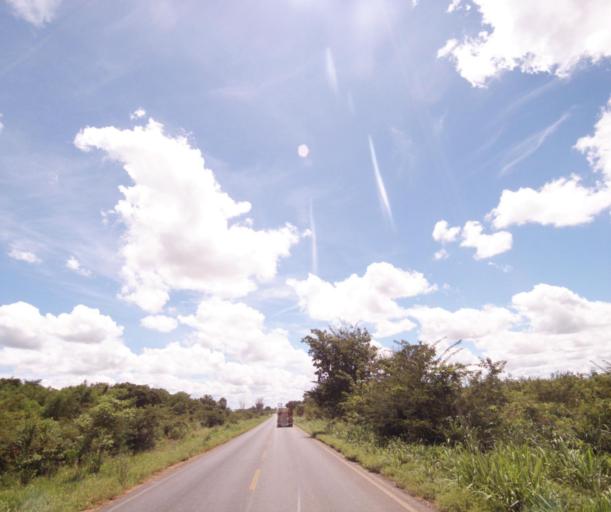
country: BR
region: Bahia
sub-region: Bom Jesus Da Lapa
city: Bom Jesus da Lapa
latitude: -13.2633
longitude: -43.5507
